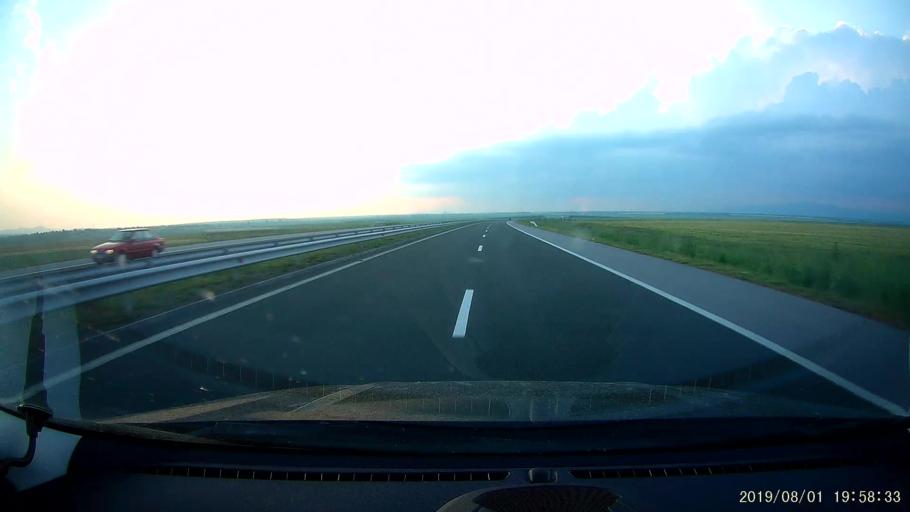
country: BG
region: Yambol
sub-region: Obshtina Straldzha
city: Straldzha
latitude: 42.5452
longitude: 26.7613
